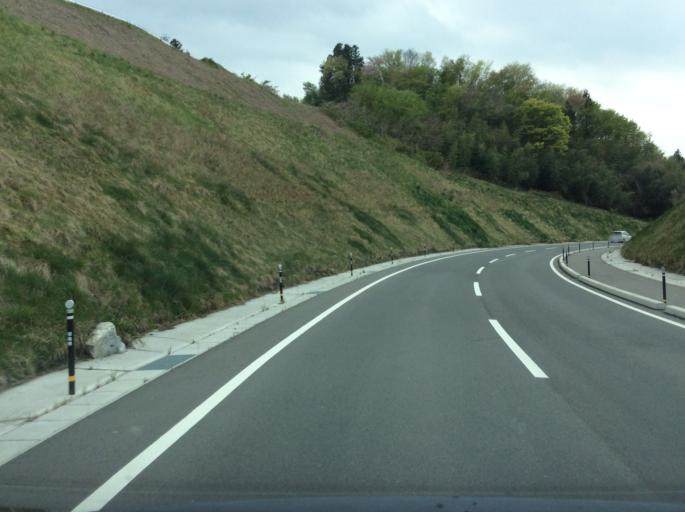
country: JP
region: Fukushima
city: Miharu
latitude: 37.4012
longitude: 140.5289
